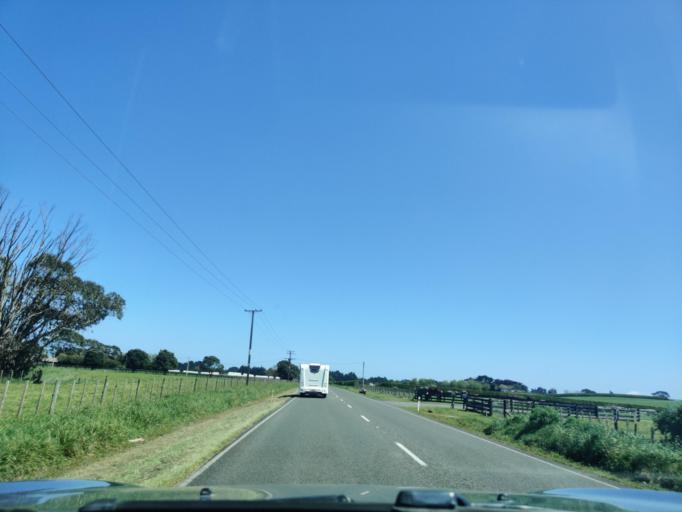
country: NZ
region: Manawatu-Wanganui
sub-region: Wanganui District
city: Wanganui
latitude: -39.8108
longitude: 174.7802
